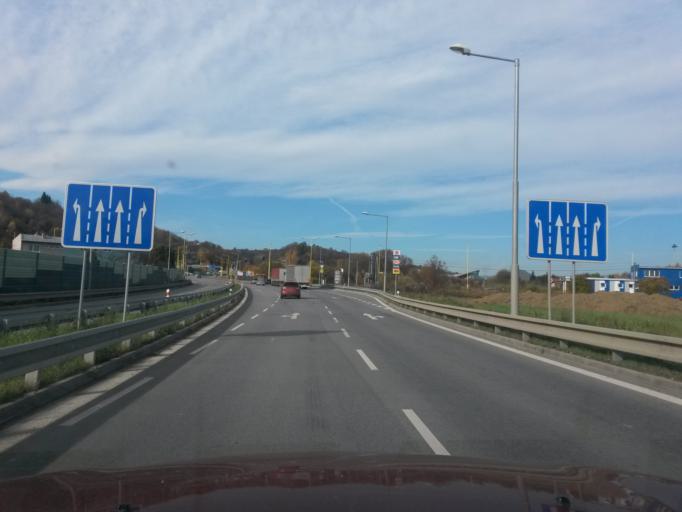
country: SK
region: Presovsky
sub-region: Okres Presov
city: Presov
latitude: 48.9823
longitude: 21.2365
